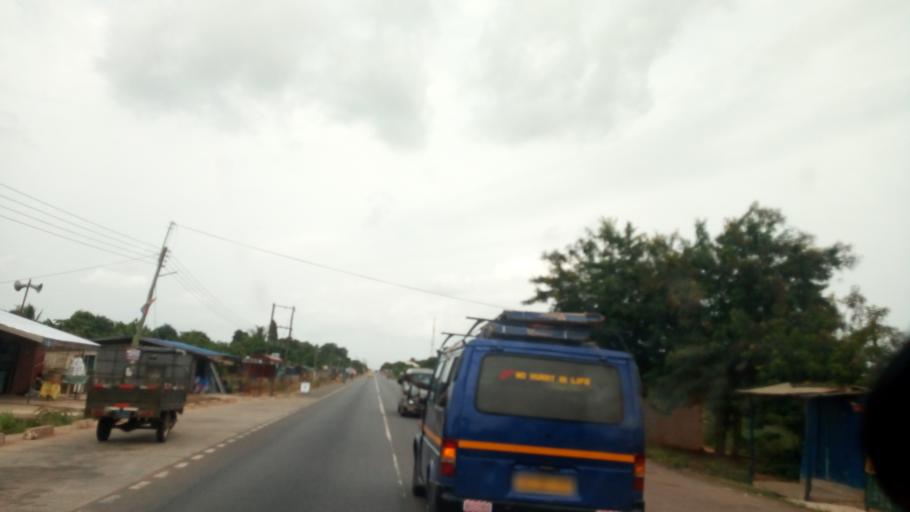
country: GH
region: Volta
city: Keta
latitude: 6.0641
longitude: 0.9094
